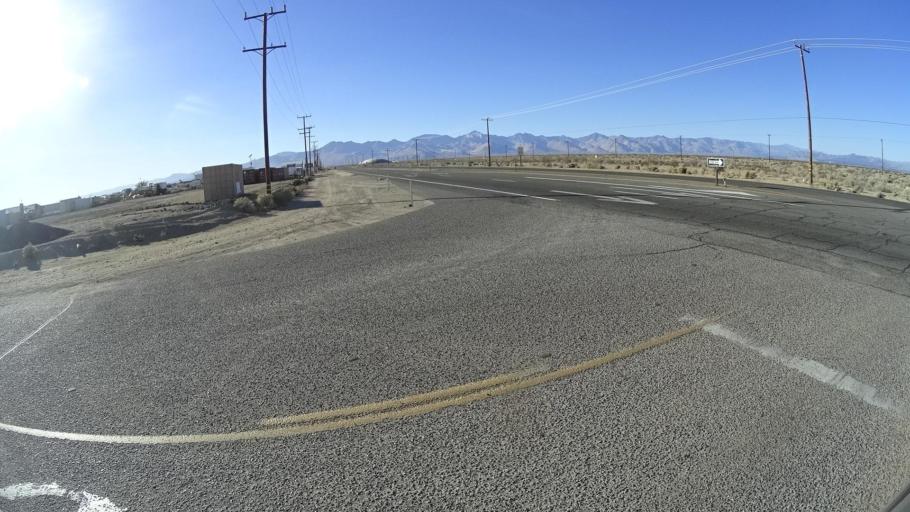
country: US
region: California
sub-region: Kern County
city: Ridgecrest
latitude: 35.6515
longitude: -117.7055
